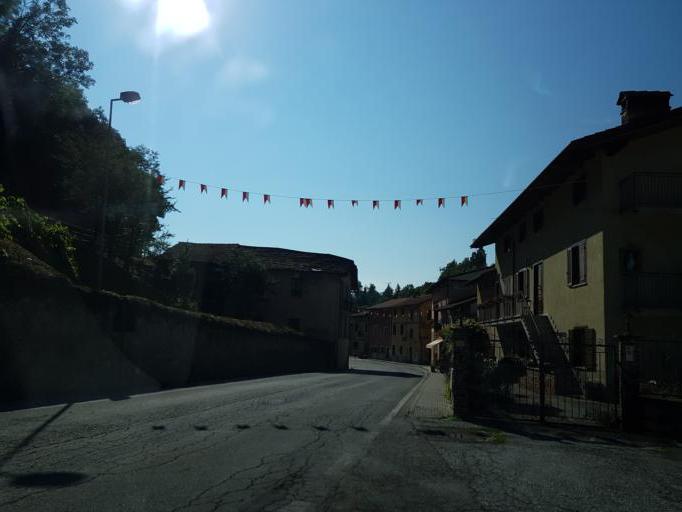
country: IT
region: Piedmont
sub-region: Provincia di Cuneo
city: Cartignano
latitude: 44.4793
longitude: 7.2854
